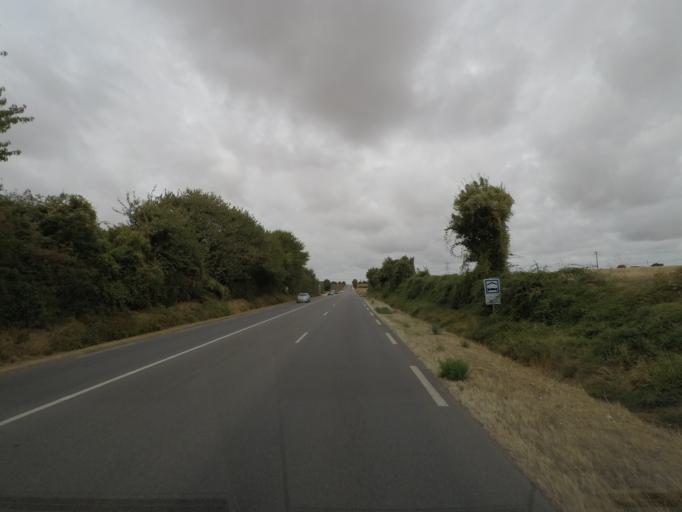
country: FR
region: Poitou-Charentes
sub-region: Departement des Deux-Sevres
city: Celles-sur-Belle
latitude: 46.2708
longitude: -0.2311
